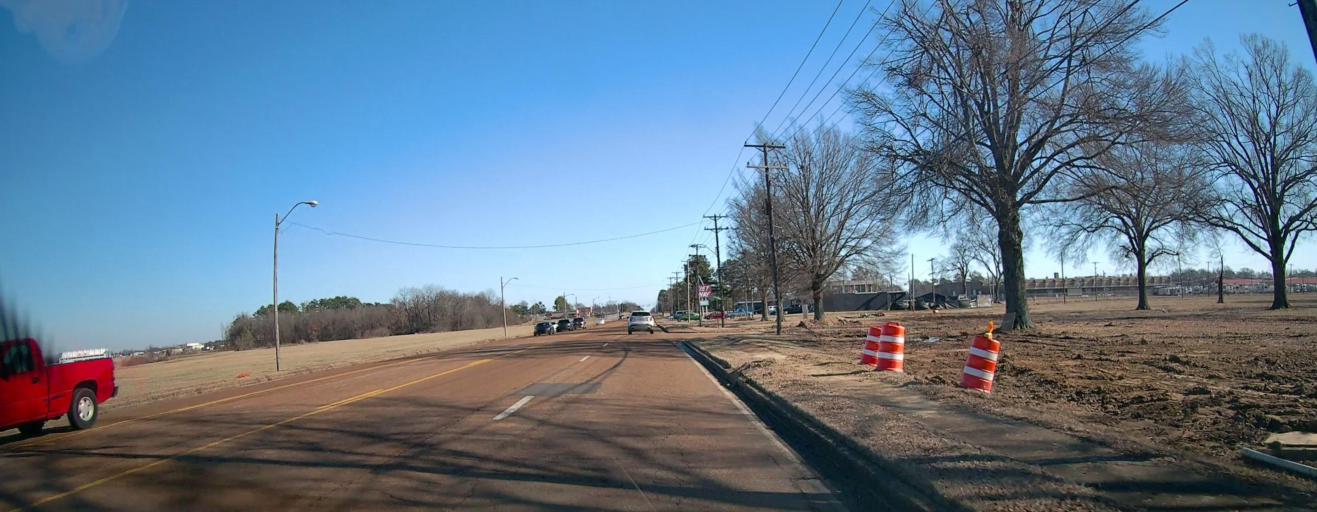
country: US
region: Tennessee
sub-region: Shelby County
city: Millington
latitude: 35.3411
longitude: -89.8847
